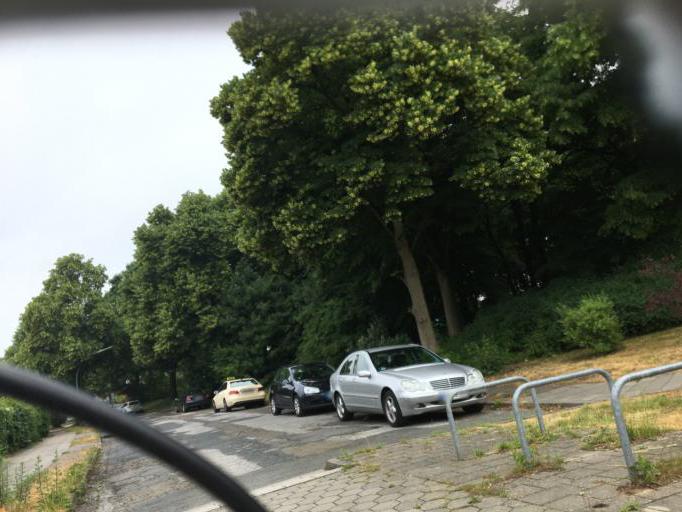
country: DE
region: Hamburg
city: Eidelstedt
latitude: 53.5779
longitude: 9.8659
